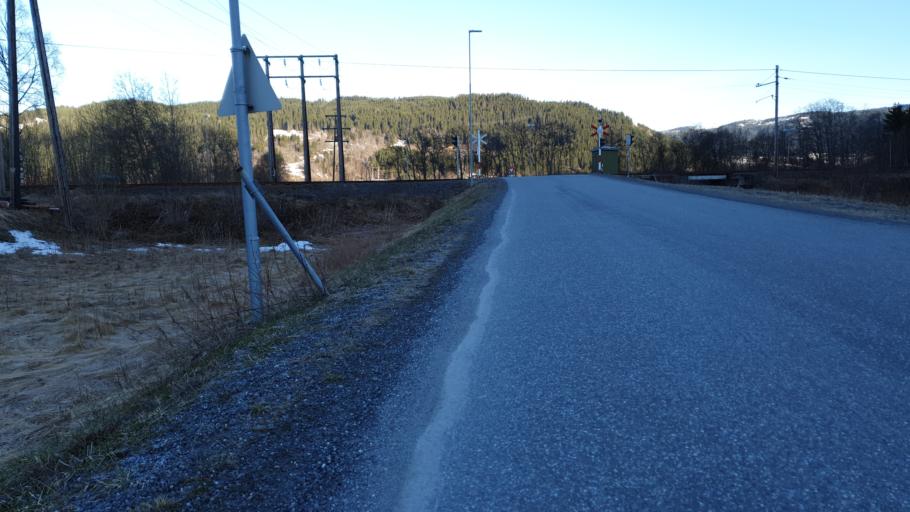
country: NO
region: Sor-Trondelag
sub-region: Orkdal
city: Orkanger
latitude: 63.2903
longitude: 9.8439
